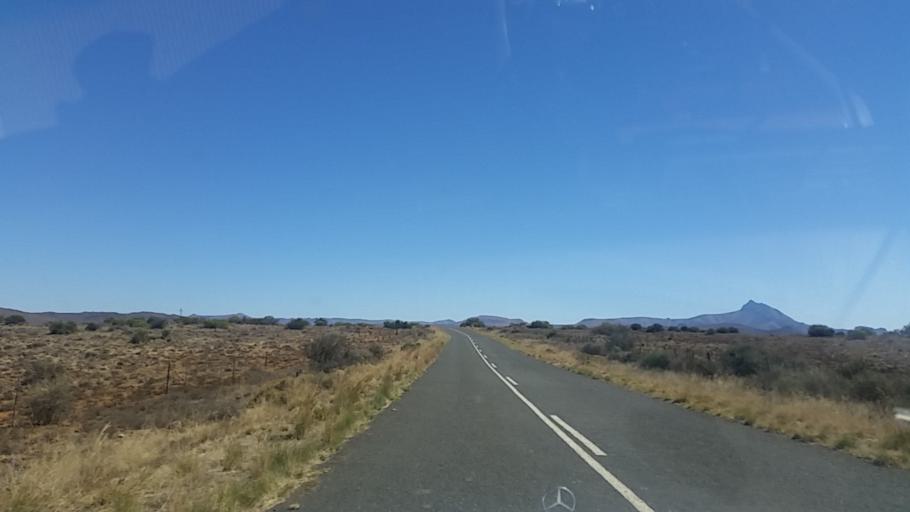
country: ZA
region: Eastern Cape
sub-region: Cacadu District Municipality
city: Graaff-Reinet
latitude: -31.9073
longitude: 24.5948
